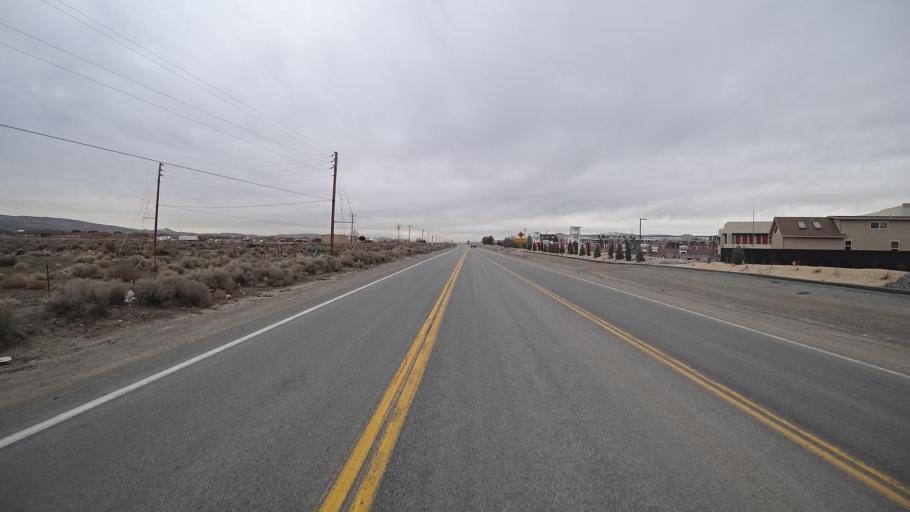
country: US
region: Nevada
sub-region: Washoe County
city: Spanish Springs
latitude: 39.6751
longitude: -119.7013
